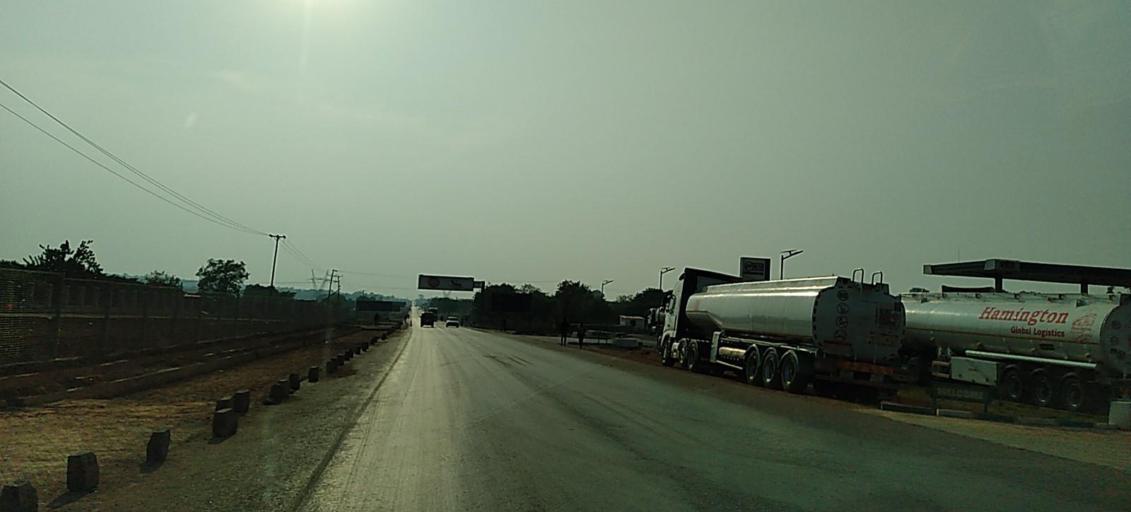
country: ZM
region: North-Western
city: Solwezi
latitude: -12.1936
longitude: 26.4487
